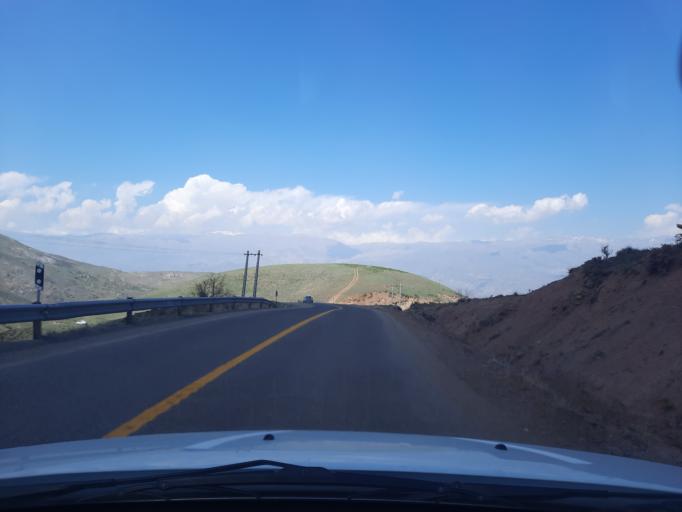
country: IR
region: Qazvin
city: Qazvin
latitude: 36.4002
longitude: 50.2200
